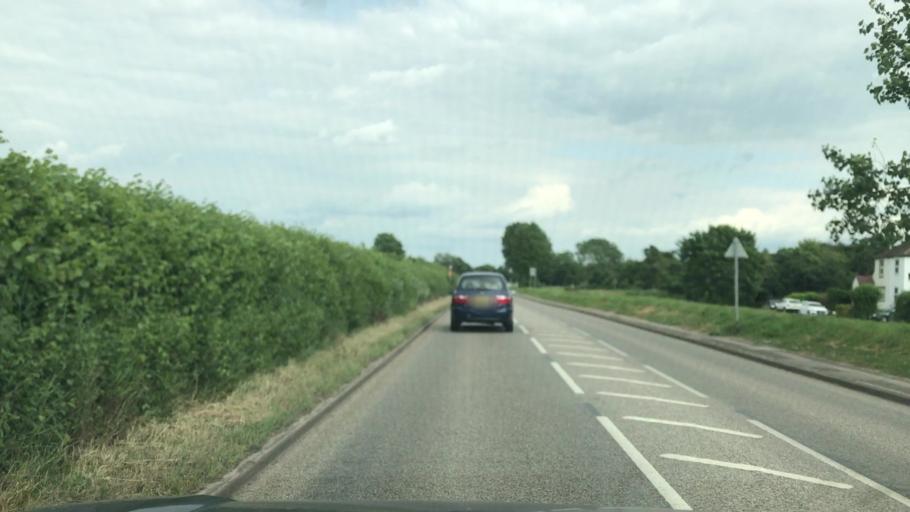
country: GB
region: England
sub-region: Kent
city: Stone
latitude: 51.4160
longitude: 0.2650
